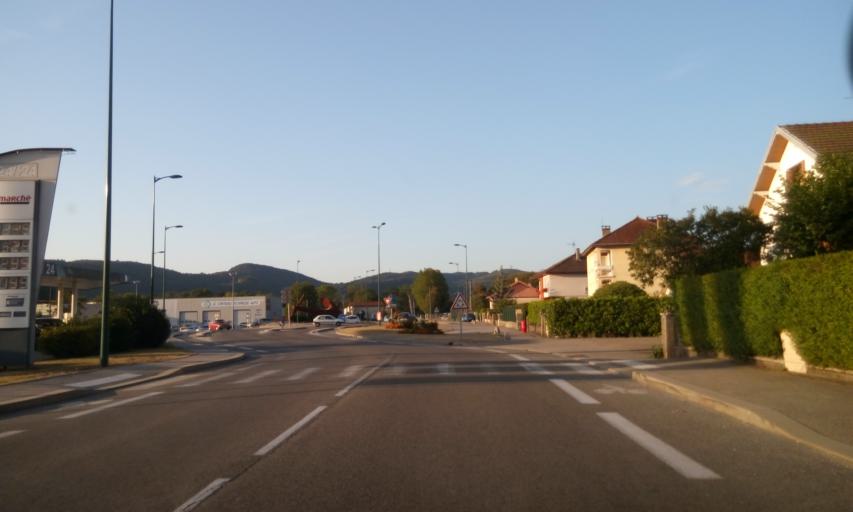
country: FR
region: Rhone-Alpes
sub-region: Departement de l'Ain
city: Montreal-la-Cluse
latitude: 46.1648
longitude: 5.5714
